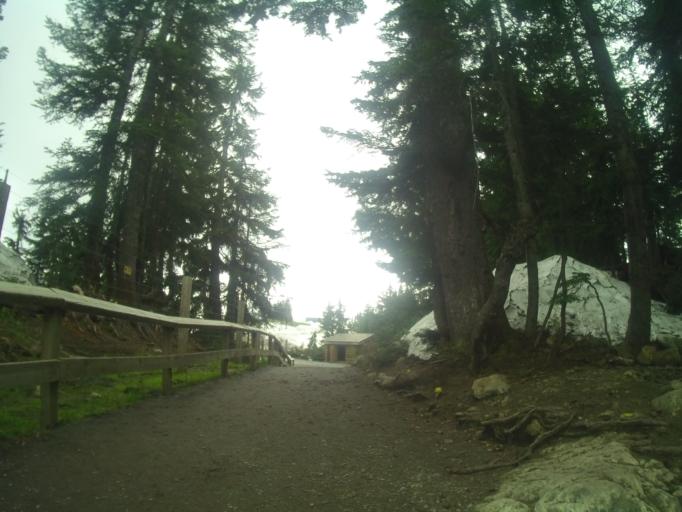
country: CA
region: British Columbia
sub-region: Fraser Valley Regional District
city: North Vancouver
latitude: 49.3826
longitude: -123.0793
